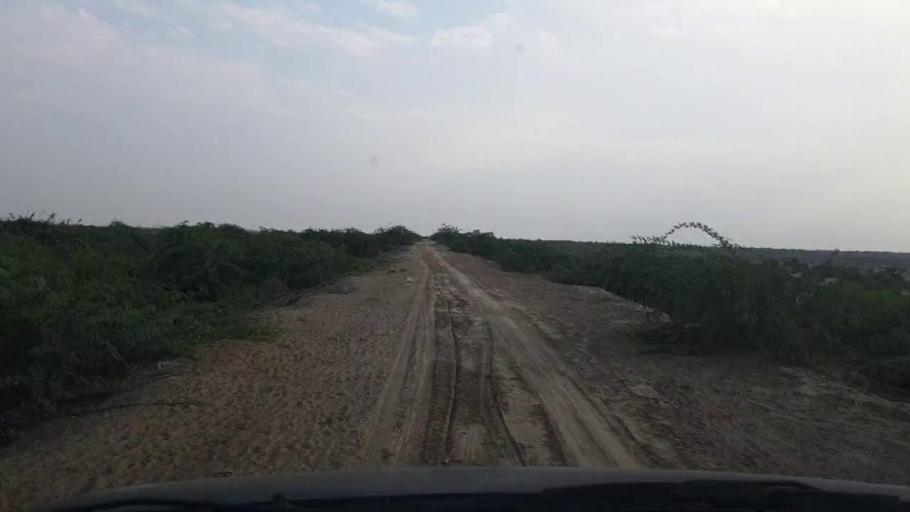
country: PK
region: Sindh
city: Badin
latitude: 24.4799
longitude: 68.6989
